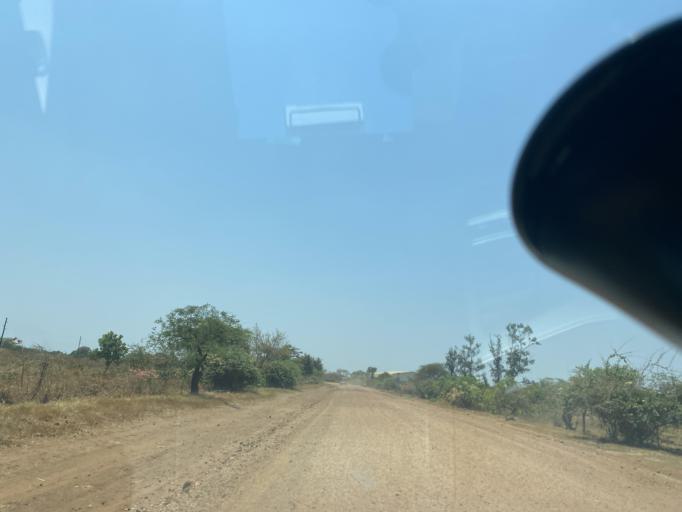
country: ZM
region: Southern
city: Nakambala
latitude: -15.4728
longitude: 27.8981
